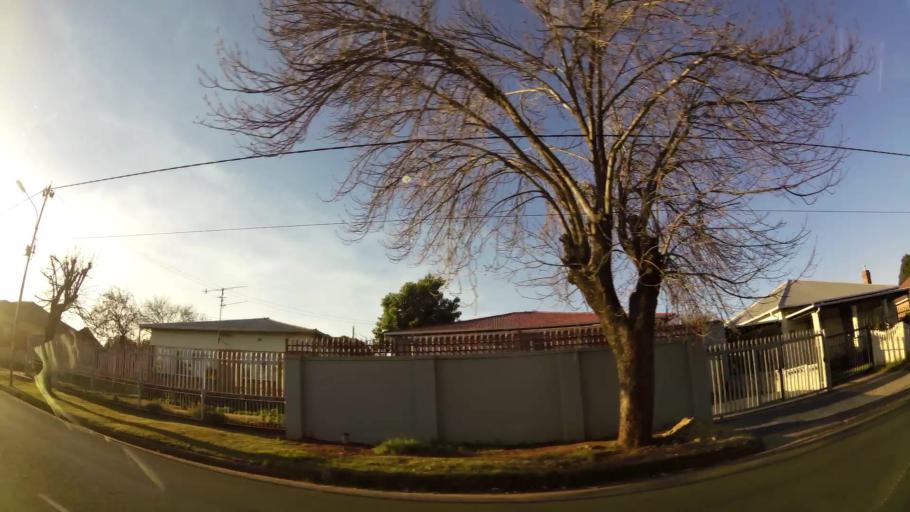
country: ZA
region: Gauteng
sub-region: City of Johannesburg Metropolitan Municipality
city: Roodepoort
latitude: -26.1605
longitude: 27.8758
